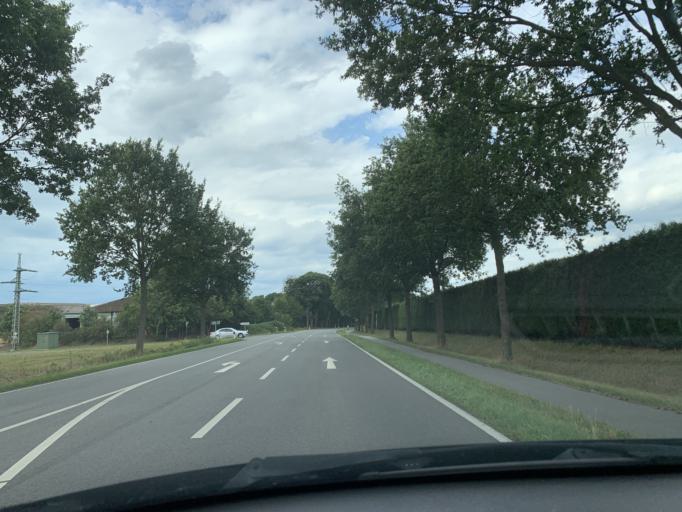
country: DE
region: Lower Saxony
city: Westerstede
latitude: 53.2338
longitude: 7.9048
